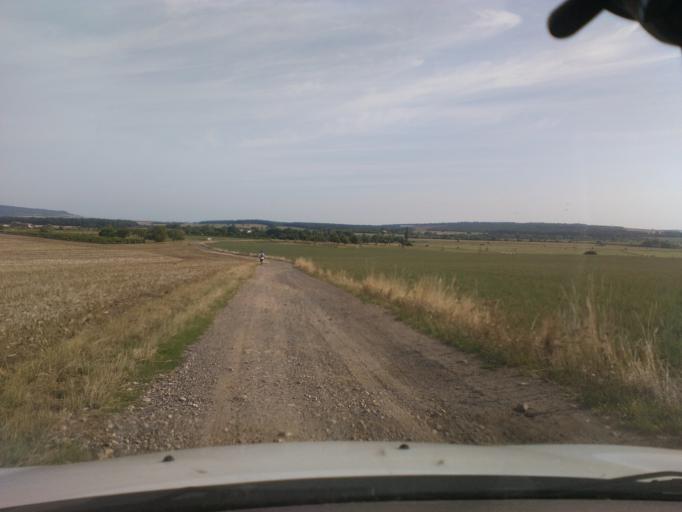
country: FR
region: Lorraine
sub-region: Departement des Vosges
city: Mirecourt
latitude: 48.3237
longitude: 6.0931
